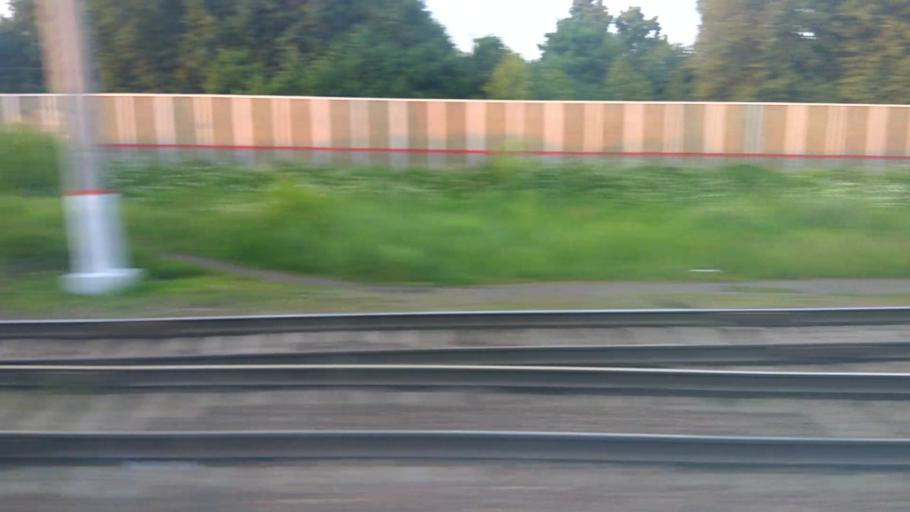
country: RU
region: Moskovskaya
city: Barybino
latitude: 55.2724
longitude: 37.8951
